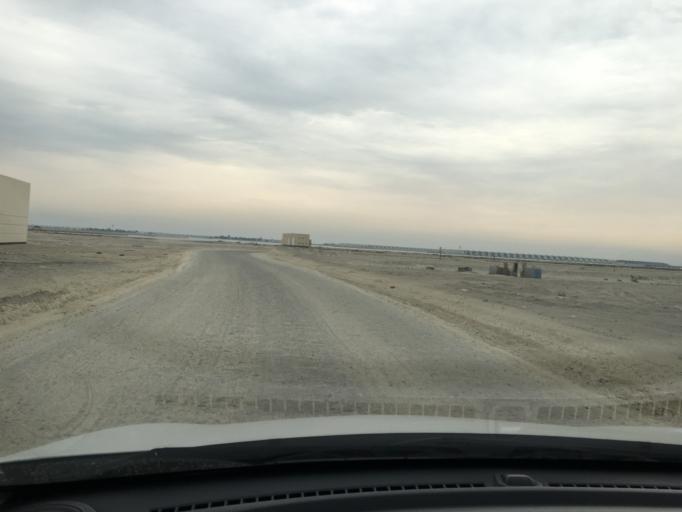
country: BH
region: Central Governorate
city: Dar Kulayb
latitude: 25.8372
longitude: 50.5911
